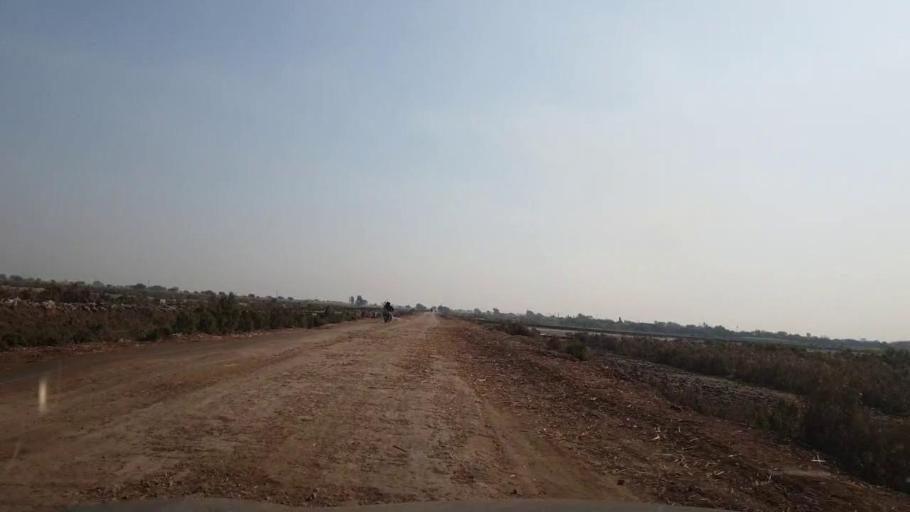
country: PK
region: Sindh
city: Berani
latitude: 25.6464
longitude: 68.8872
